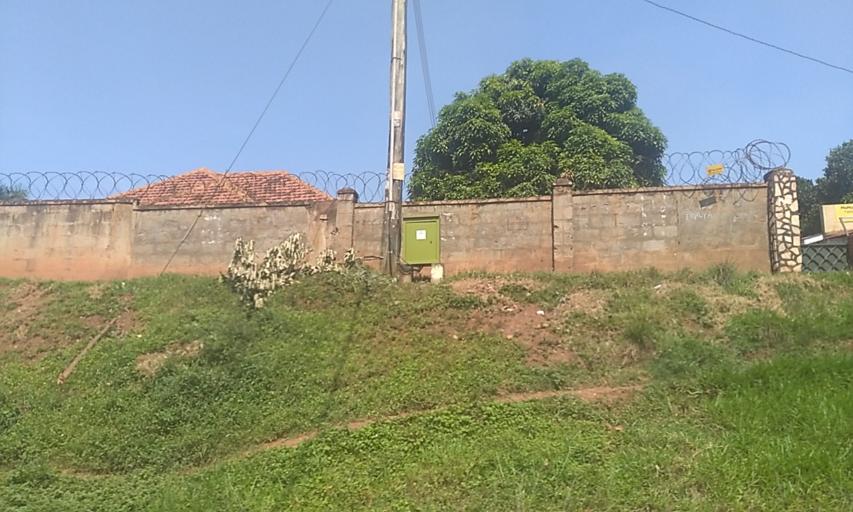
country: UG
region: Central Region
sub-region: Wakiso District
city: Kireka
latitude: 0.3638
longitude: 32.6060
